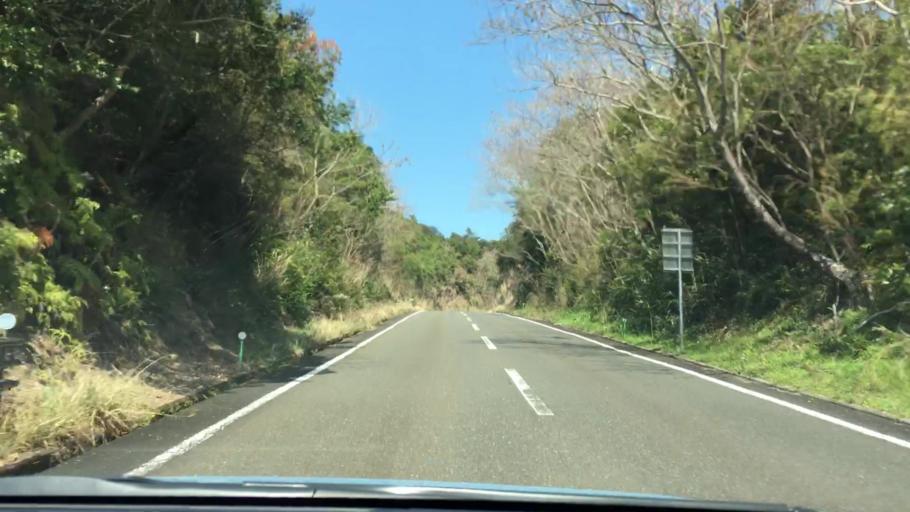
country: JP
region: Mie
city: Toba
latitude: 34.4404
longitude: 136.9110
